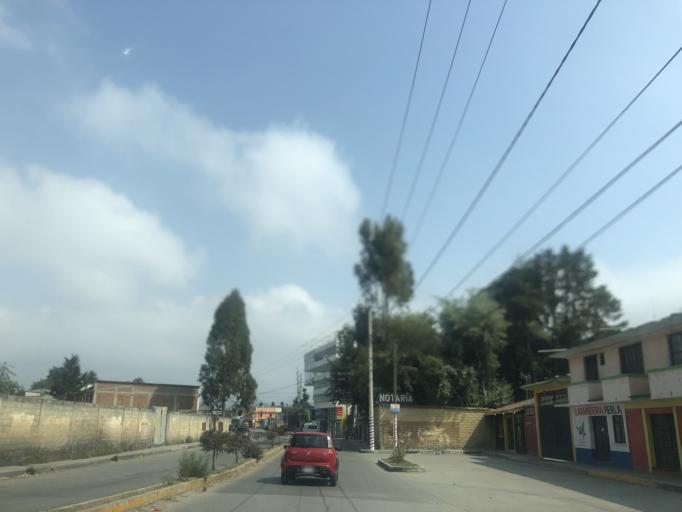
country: MX
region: Chiapas
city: San Cristobal de las Casas
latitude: 16.7127
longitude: -92.6335
